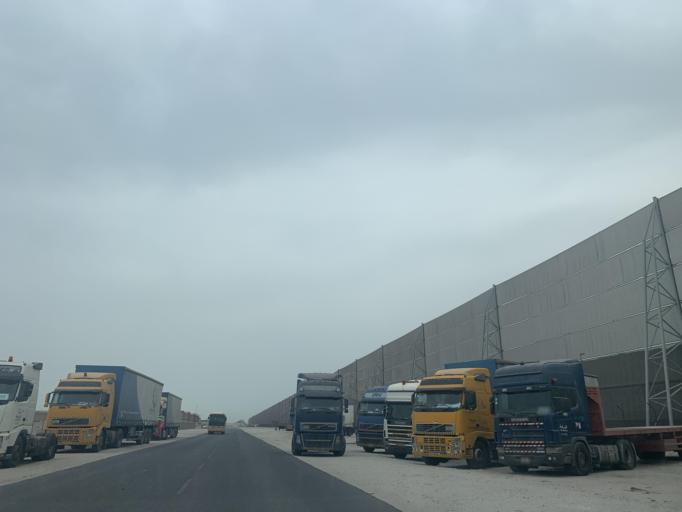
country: BH
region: Muharraq
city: Al Hadd
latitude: 26.2072
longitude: 50.6799
